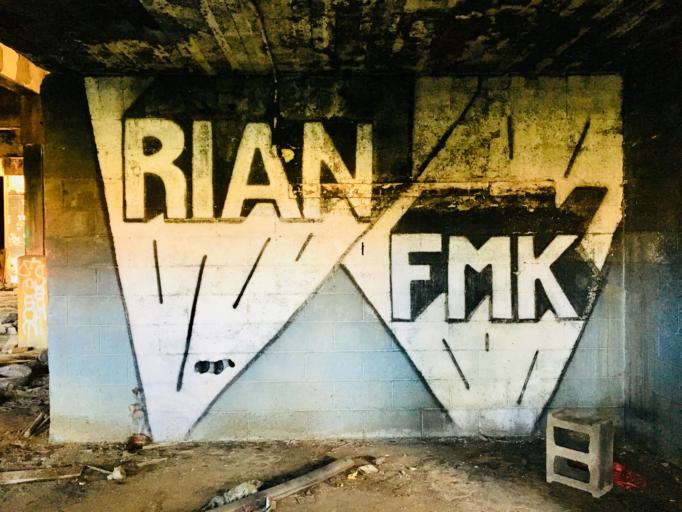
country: US
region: Michigan
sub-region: Wayne County
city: Hamtramck
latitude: 42.3783
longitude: -83.0237
